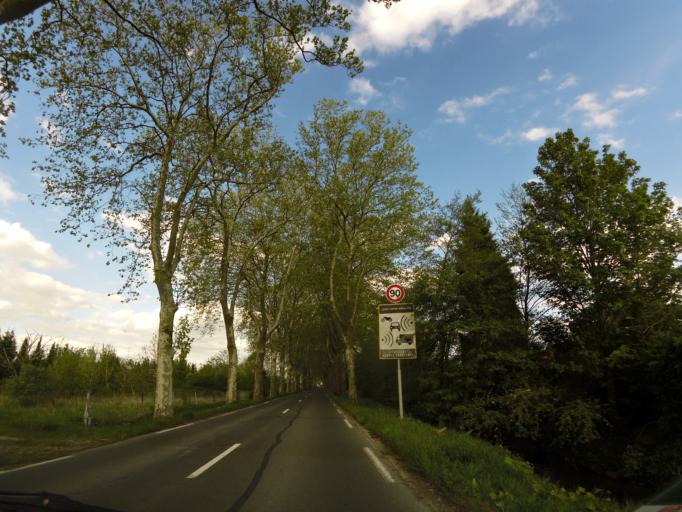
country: FR
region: Midi-Pyrenees
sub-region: Departement de la Haute-Garonne
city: Revel
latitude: 43.4533
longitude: 2.0250
